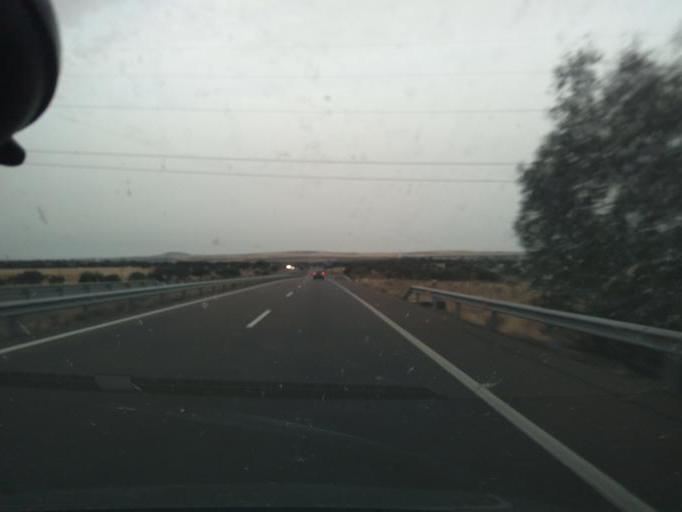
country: ES
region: Extremadura
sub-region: Provincia de Badajoz
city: Trujillanos
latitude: 38.9509
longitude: -6.2235
